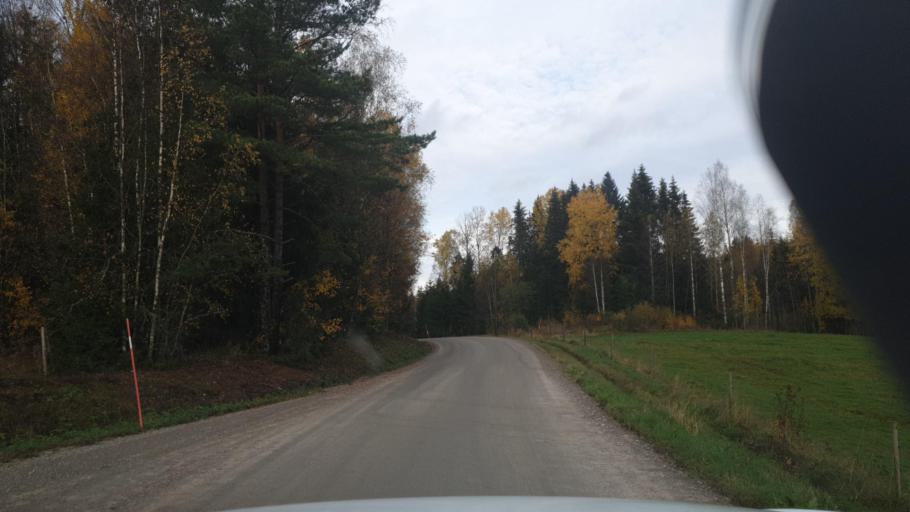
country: SE
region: Vaermland
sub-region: Sunne Kommun
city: Sunne
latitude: 59.6843
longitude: 12.8926
